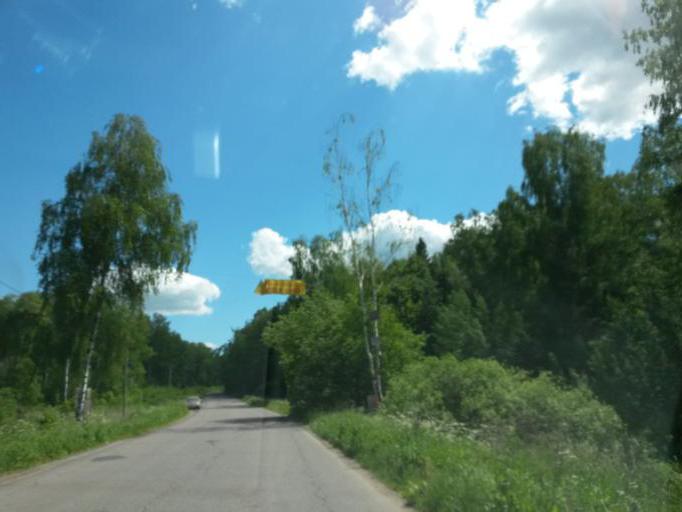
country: RU
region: Moskovskaya
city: L'vovskiy
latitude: 55.3169
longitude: 37.6123
